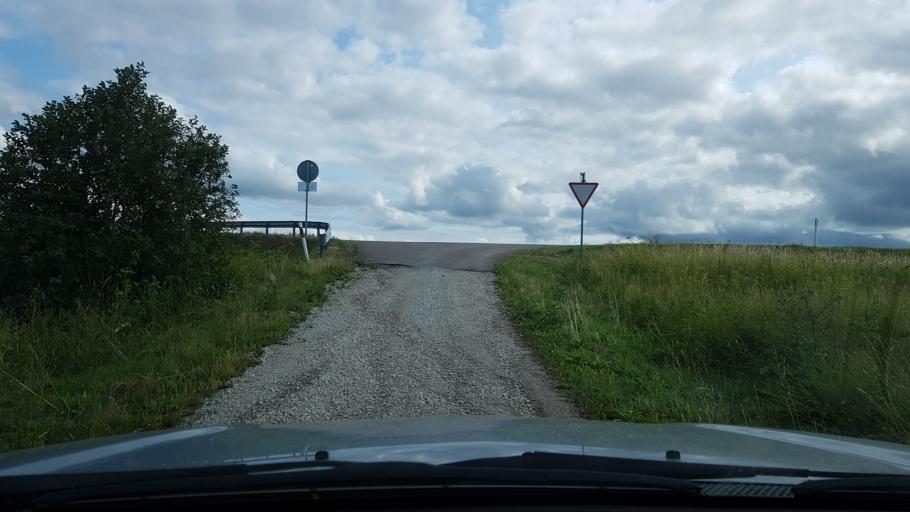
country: EE
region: Ida-Virumaa
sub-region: Narva-Joesuu linn
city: Narva-Joesuu
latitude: 59.4093
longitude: 28.0365
